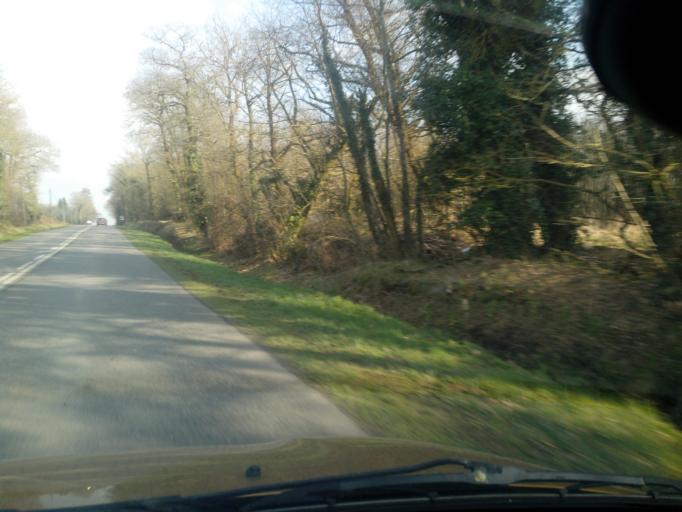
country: FR
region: Brittany
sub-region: Departement du Morbihan
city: La Vraie-Croix
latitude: 47.6972
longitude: -2.5232
